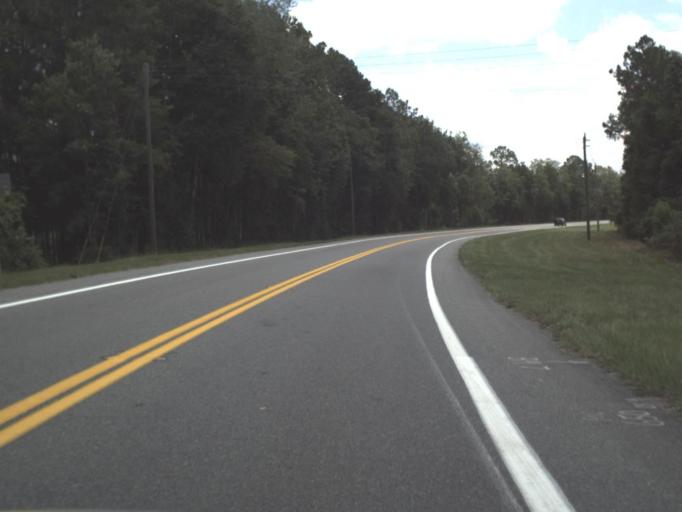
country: US
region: Florida
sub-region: Union County
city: Lake Butler
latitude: 30.0467
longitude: -82.3027
